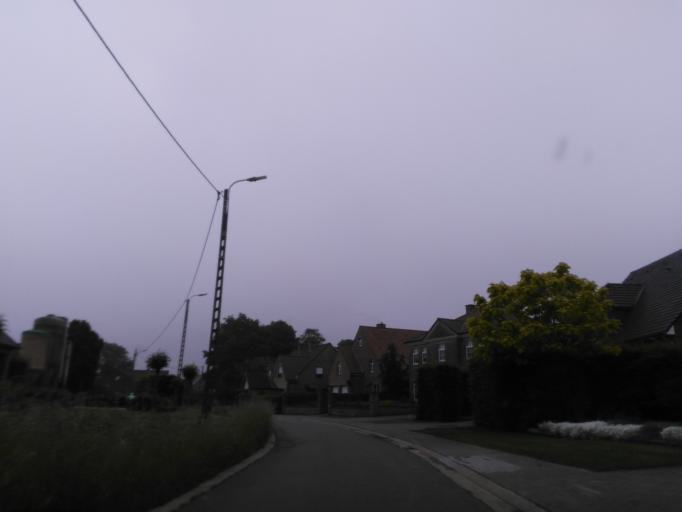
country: BE
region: Flanders
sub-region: Provincie Oost-Vlaanderen
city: Sint-Gillis-Waas
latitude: 51.2261
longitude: 4.1859
